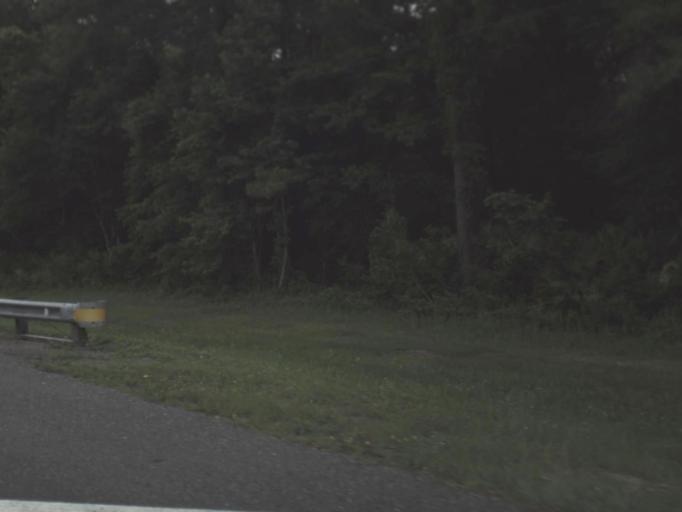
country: US
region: Florida
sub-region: Nassau County
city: Nassau Village-Ratliff
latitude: 30.5043
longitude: -81.7911
